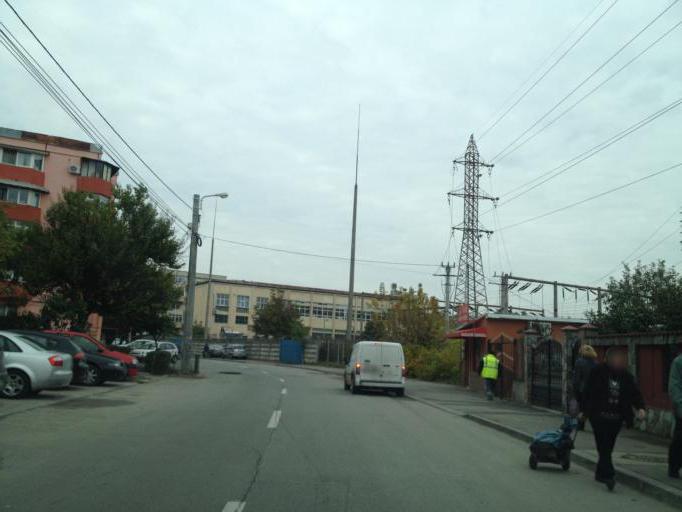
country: RO
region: Dolj
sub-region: Municipiul Craiova
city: Popoveni
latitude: 44.3023
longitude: 23.7898
